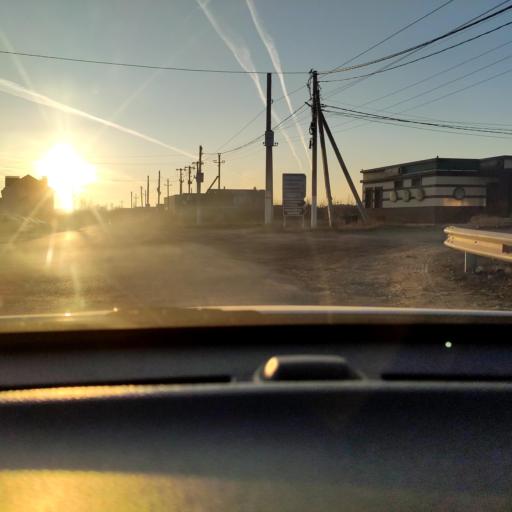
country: RU
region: Voronezj
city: Somovo
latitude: 51.6759
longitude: 39.3331
